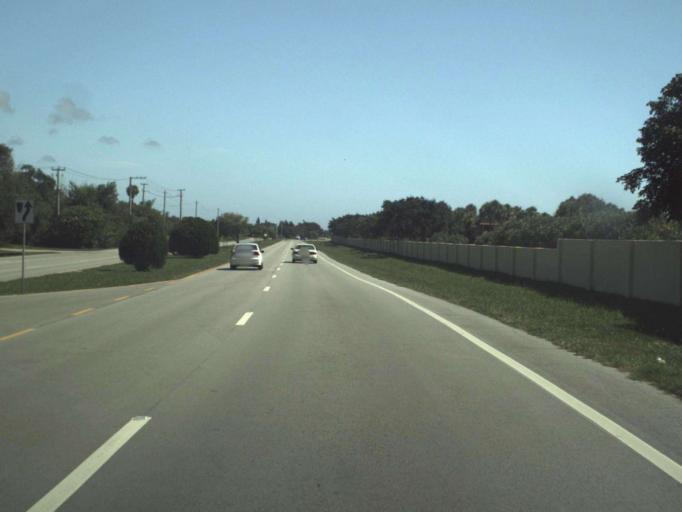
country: US
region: Florida
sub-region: Indian River County
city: Florida Ridge
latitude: 27.6103
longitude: -80.3814
